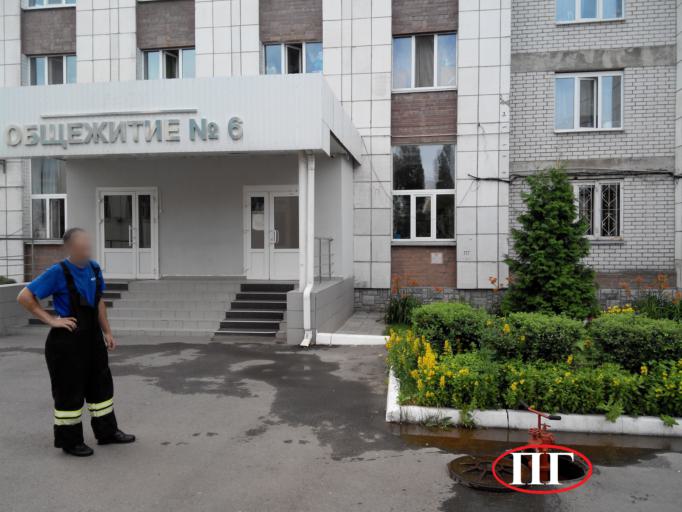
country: RU
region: Voronezj
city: Voronezh
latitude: 51.6491
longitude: 39.1933
